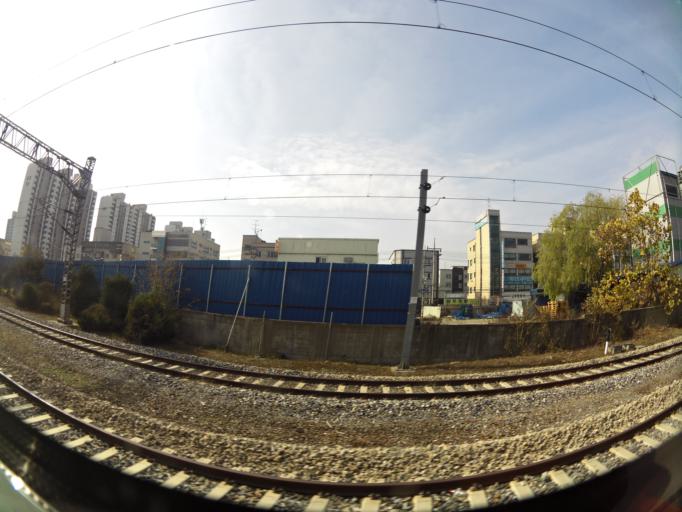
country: KR
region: Daejeon
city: Songgang-dong
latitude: 36.6046
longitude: 127.2949
